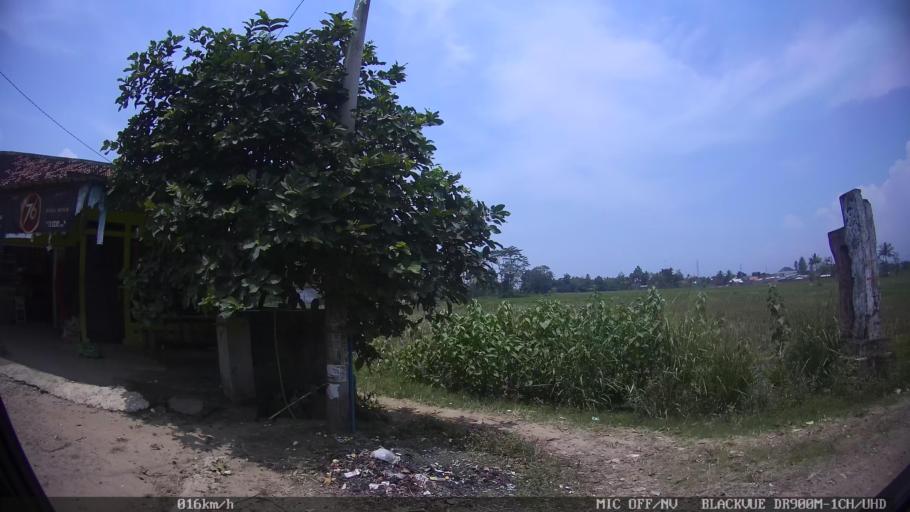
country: ID
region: Lampung
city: Kedaton
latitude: -5.3292
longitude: 105.2478
